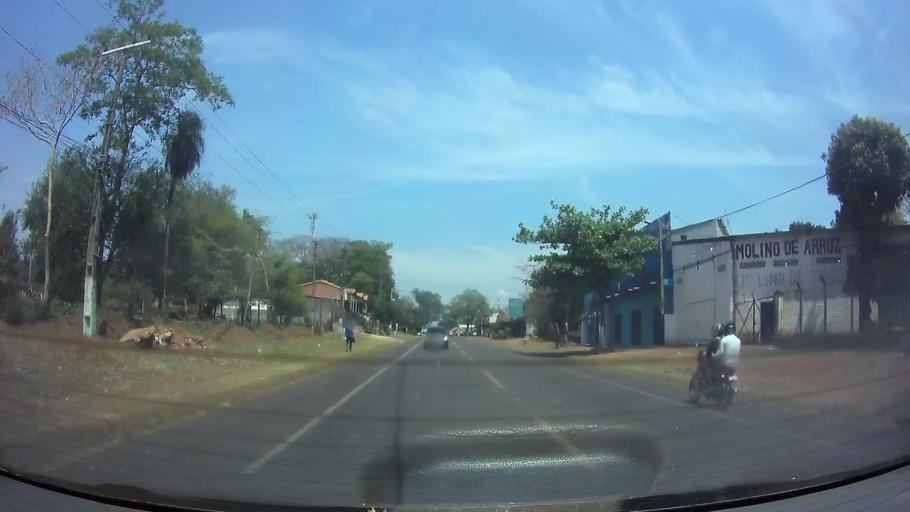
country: PY
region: Central
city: Guarambare
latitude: -25.4286
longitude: -57.4506
